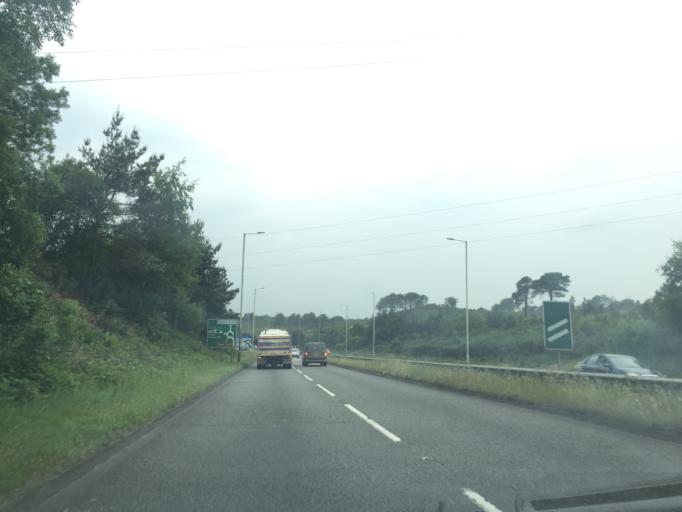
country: GB
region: England
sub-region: Dorset
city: Parkstone
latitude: 50.7533
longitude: -1.9443
